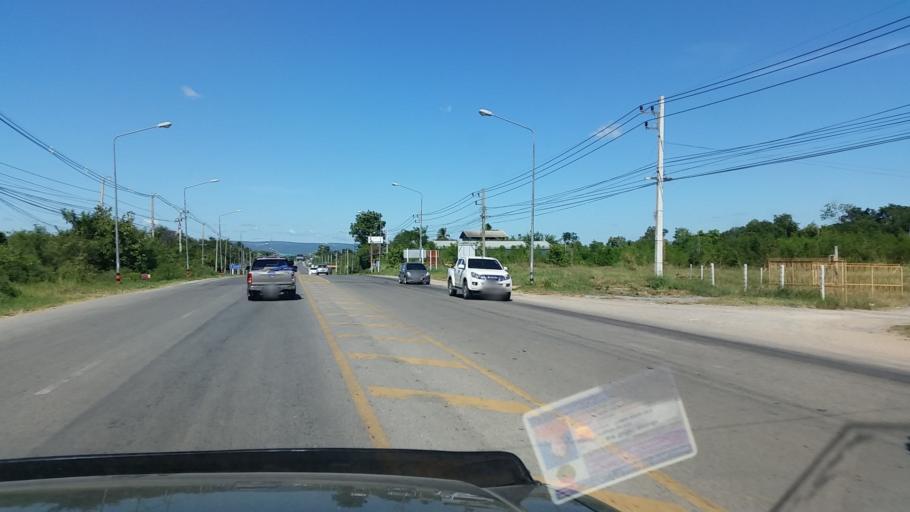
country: TH
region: Chaiyaphum
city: Chaiyaphum
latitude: 15.8520
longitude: 102.0205
